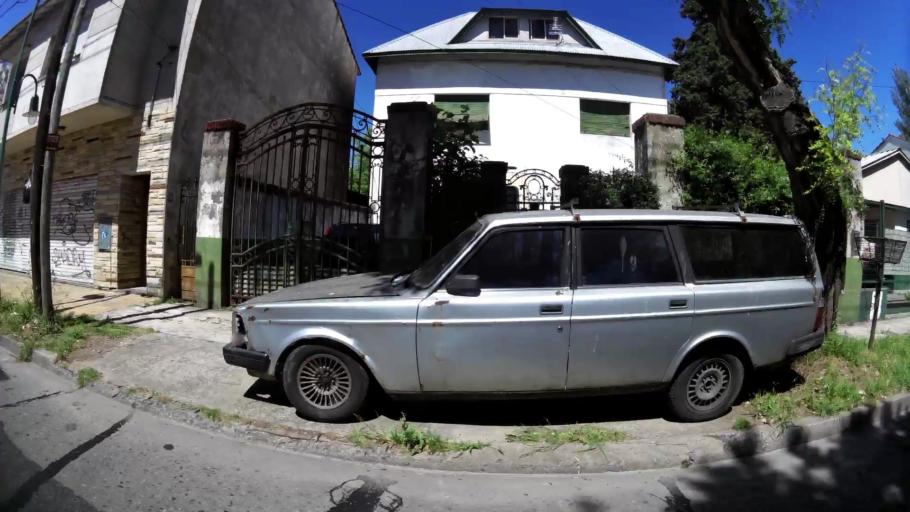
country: AR
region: Buenos Aires
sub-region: Partido de General San Martin
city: General San Martin
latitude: -34.5297
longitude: -58.5433
